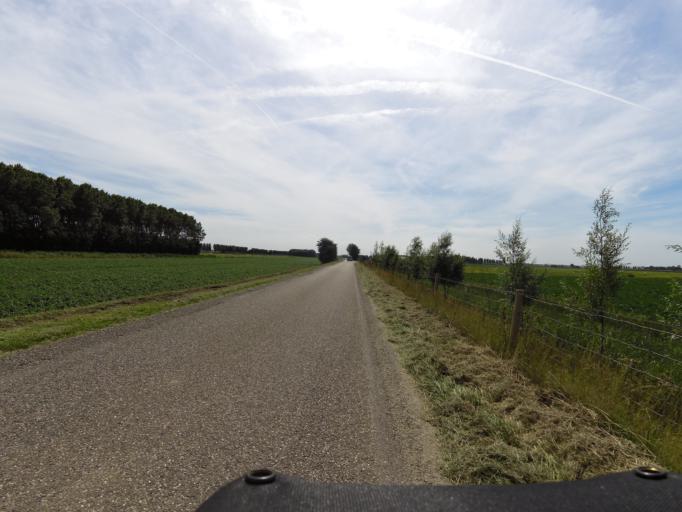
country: NL
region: South Holland
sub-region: Gemeente Goeree-Overflakkee
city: Dirksland
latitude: 51.7750
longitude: 4.1088
